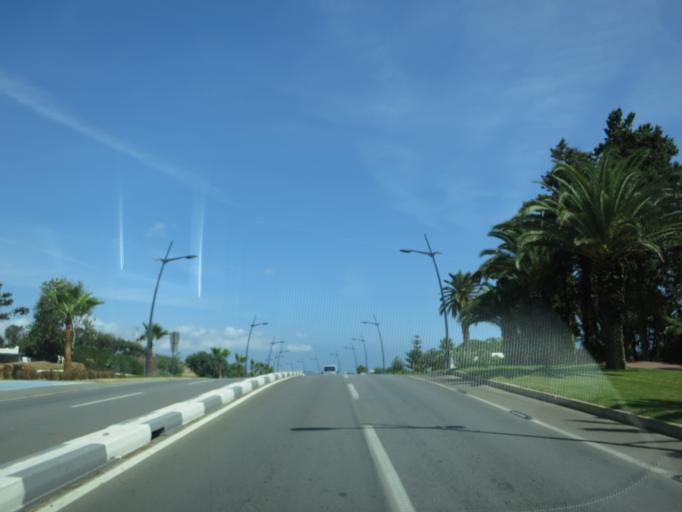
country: ES
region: Ceuta
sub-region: Ceuta
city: Ceuta
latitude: 35.7757
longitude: -5.3488
